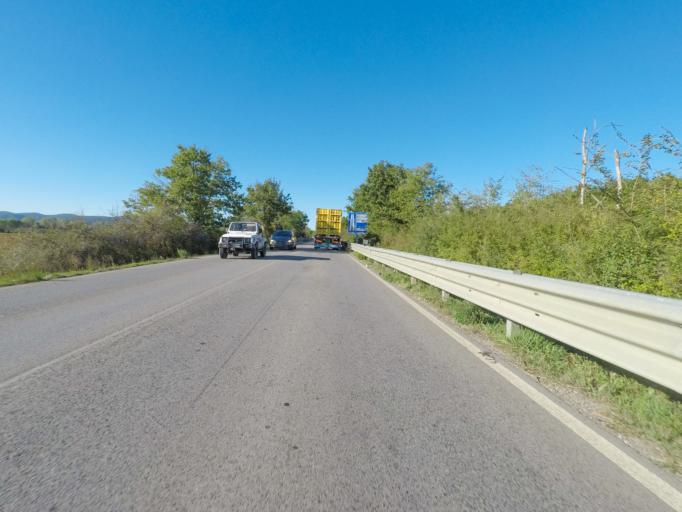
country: IT
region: Tuscany
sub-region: Provincia di Siena
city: Rosia
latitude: 43.2180
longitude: 11.2755
